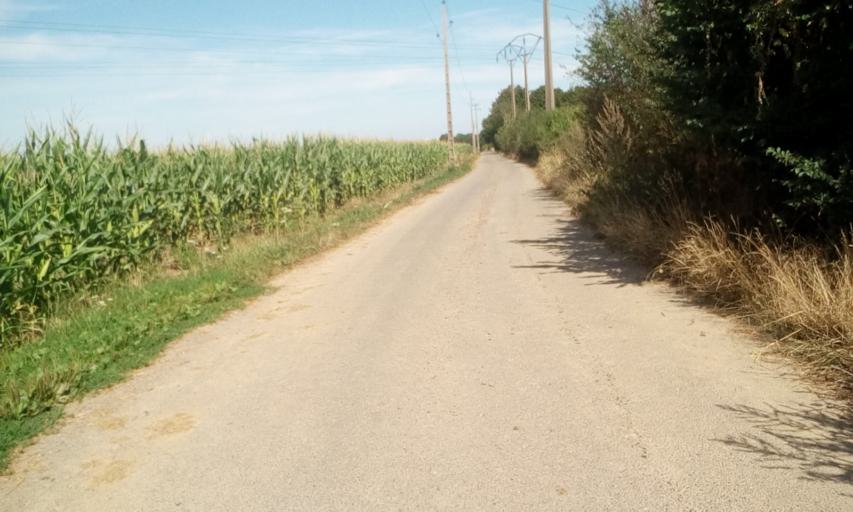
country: FR
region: Lower Normandy
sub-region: Departement du Calvados
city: Fontaine-Etoupefour
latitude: 49.1380
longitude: -0.4463
